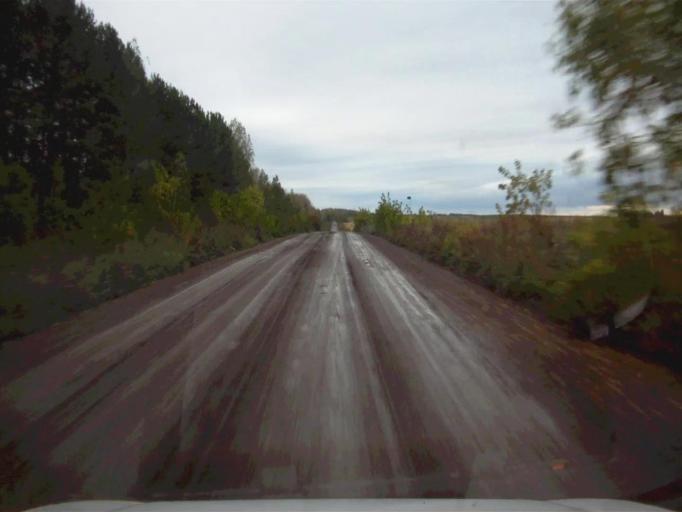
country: RU
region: Sverdlovsk
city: Mikhaylovsk
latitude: 56.1619
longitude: 59.2449
